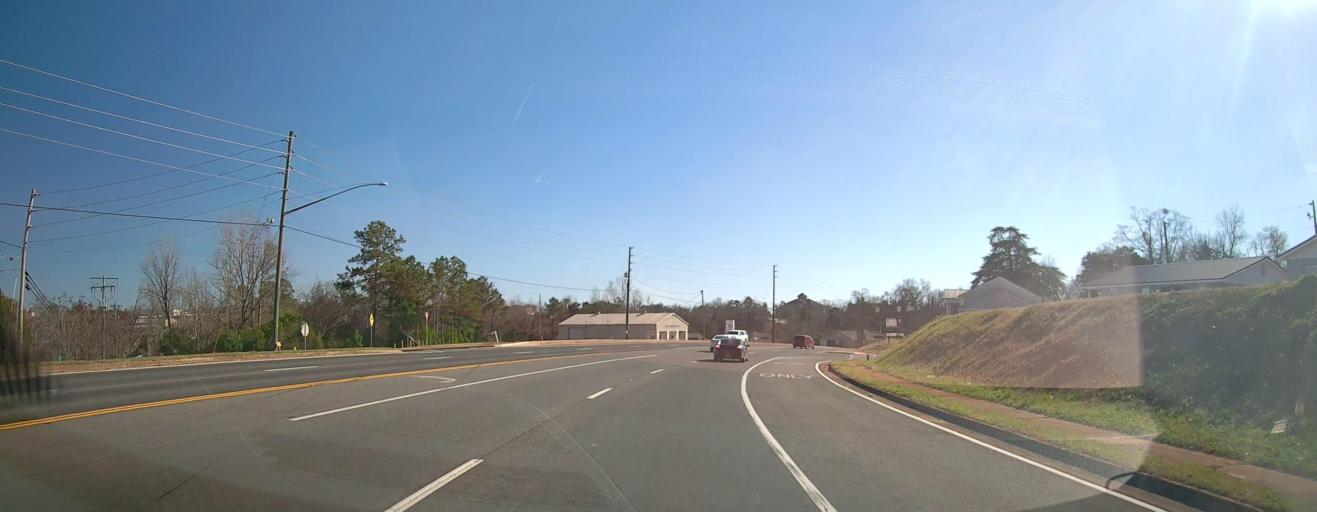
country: US
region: Georgia
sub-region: Sumter County
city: Americus
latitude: 32.0801
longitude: -84.2387
